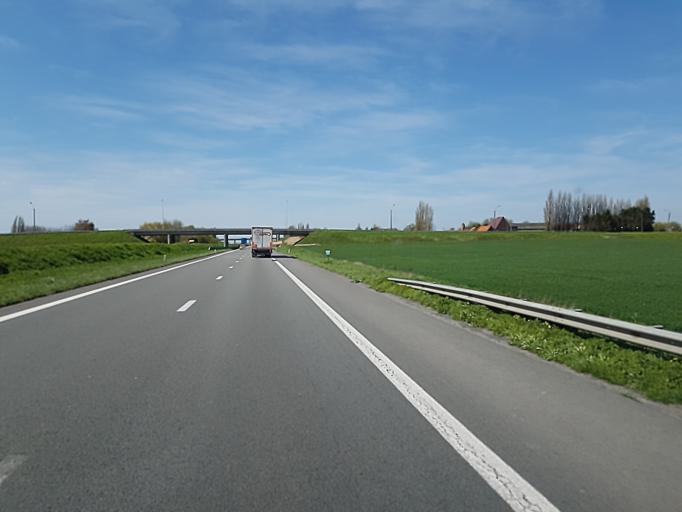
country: BE
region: Flanders
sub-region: Provincie West-Vlaanderen
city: Kortrijk
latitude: 50.7772
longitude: 3.2557
